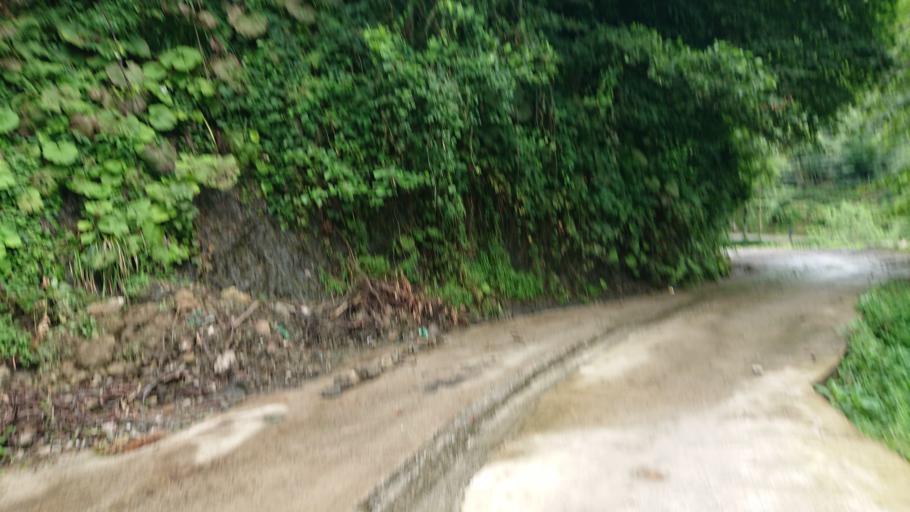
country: TR
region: Rize
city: Rize
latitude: 40.9765
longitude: 40.4854
